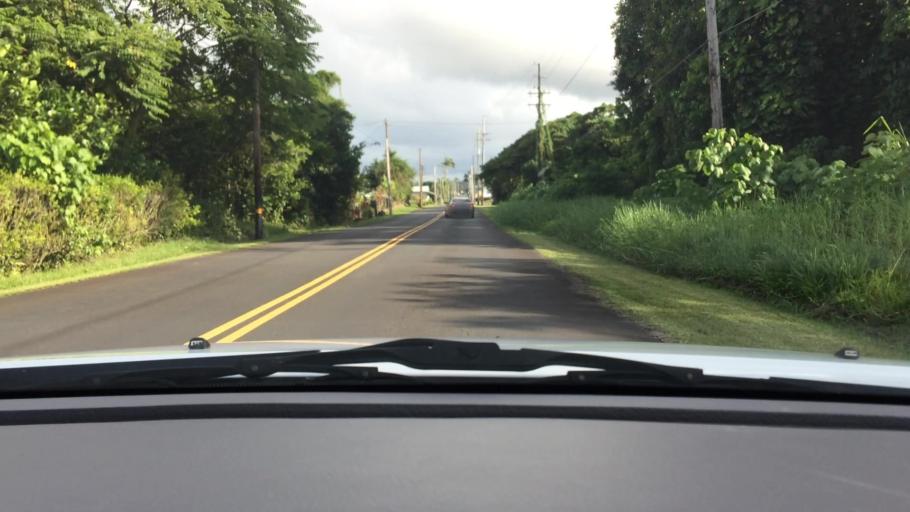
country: US
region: Hawaii
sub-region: Hawaii County
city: Hilo
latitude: 19.7152
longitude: -155.0714
